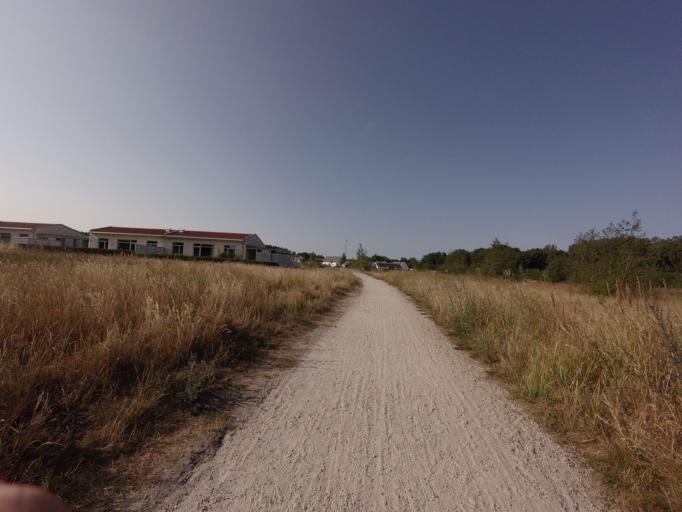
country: SE
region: Skane
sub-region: Landskrona
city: Asmundtorp
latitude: 55.8473
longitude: 12.9220
